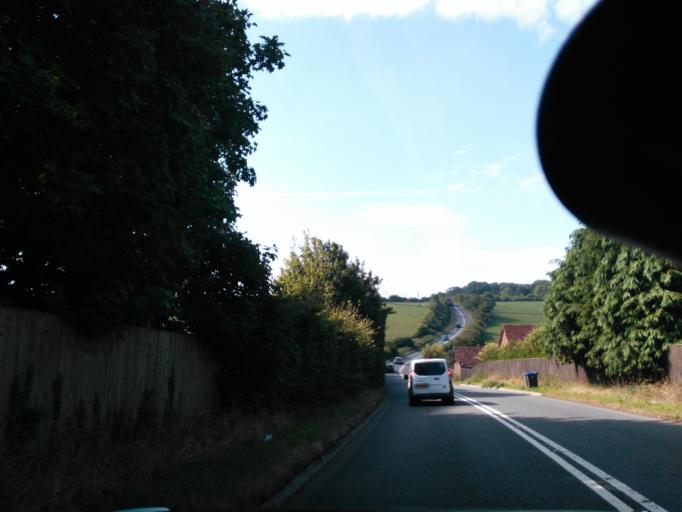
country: GB
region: England
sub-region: Wiltshire
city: Hindon
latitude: 51.0955
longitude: -2.1626
